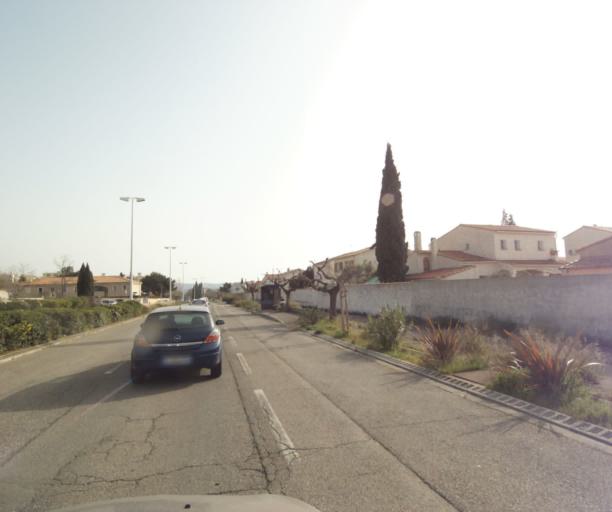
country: FR
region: Provence-Alpes-Cote d'Azur
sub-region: Departement des Bouches-du-Rhone
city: Vitrolles
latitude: 43.4518
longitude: 5.2447
